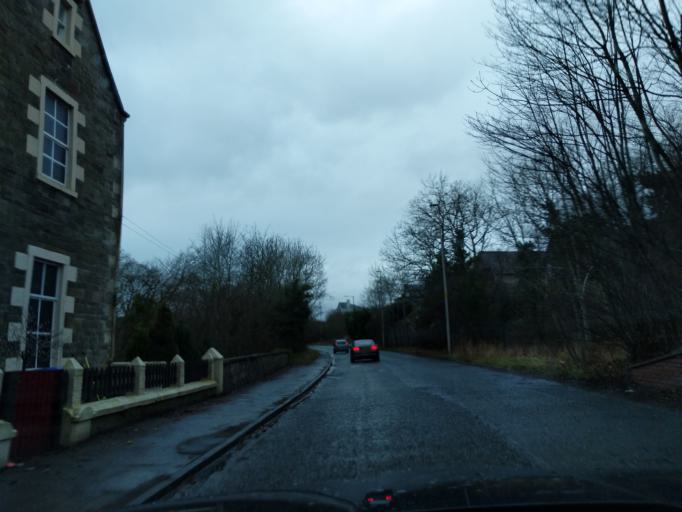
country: GB
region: Scotland
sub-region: The Scottish Borders
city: Galashiels
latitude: 55.6281
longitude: -2.8277
